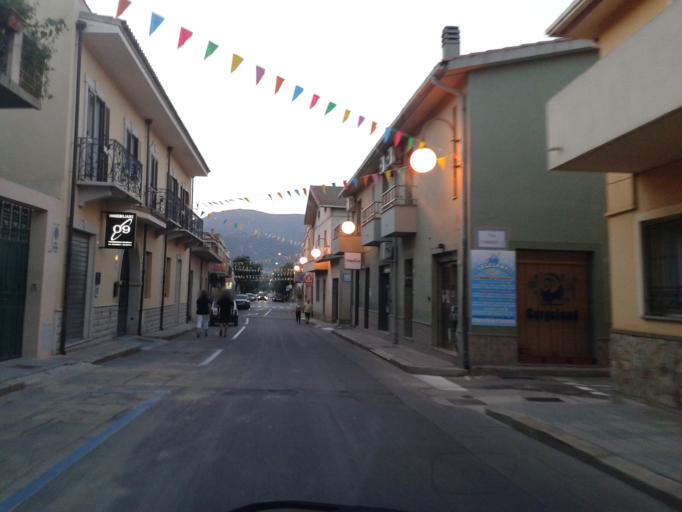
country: IT
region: Sardinia
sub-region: Provincia di Cagliari
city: Villasimius
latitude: 39.1454
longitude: 9.5172
